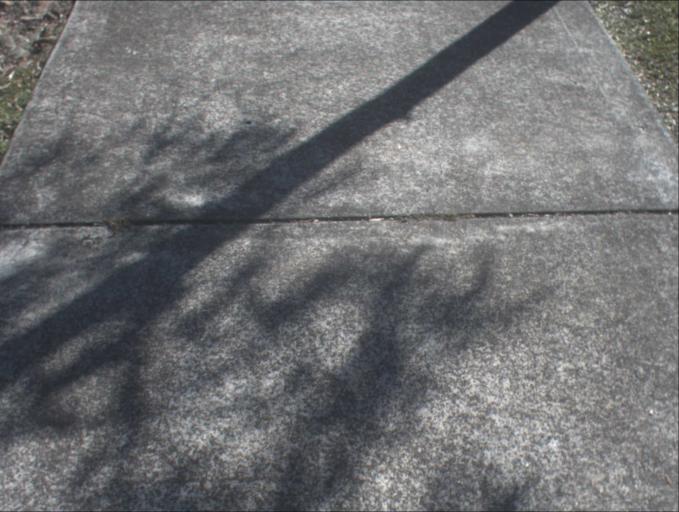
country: AU
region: Queensland
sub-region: Logan
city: Slacks Creek
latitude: -27.6344
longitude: 153.1586
